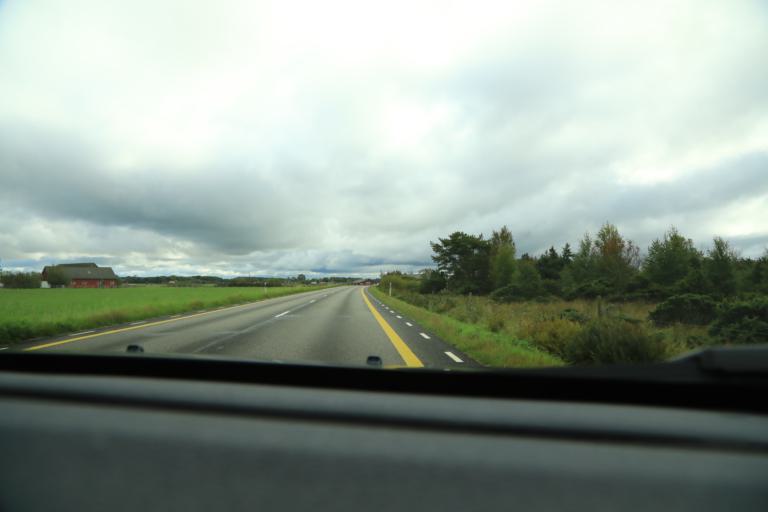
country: SE
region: Halland
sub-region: Varbergs Kommun
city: Tvaaker
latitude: 57.0195
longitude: 12.3428
